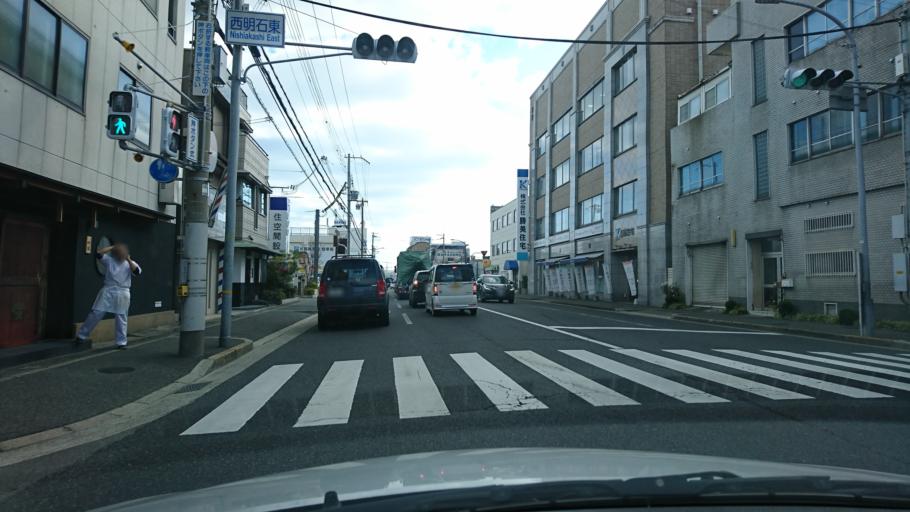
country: JP
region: Hyogo
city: Akashi
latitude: 34.6646
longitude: 134.9644
